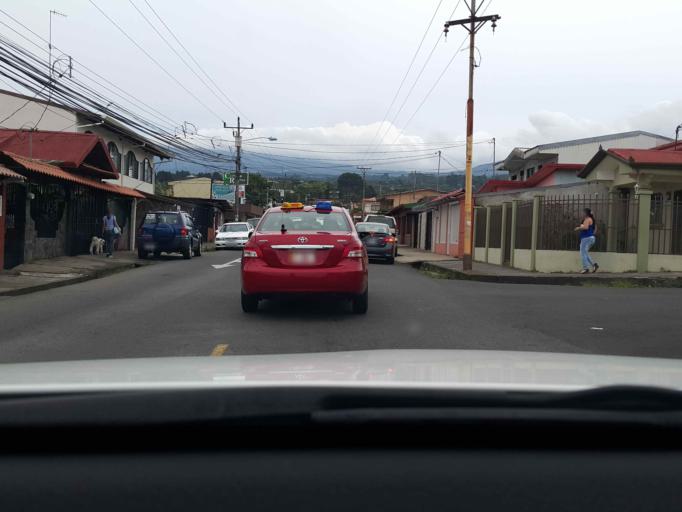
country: CR
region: Heredia
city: San Rafael
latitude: 10.0135
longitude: -84.0967
